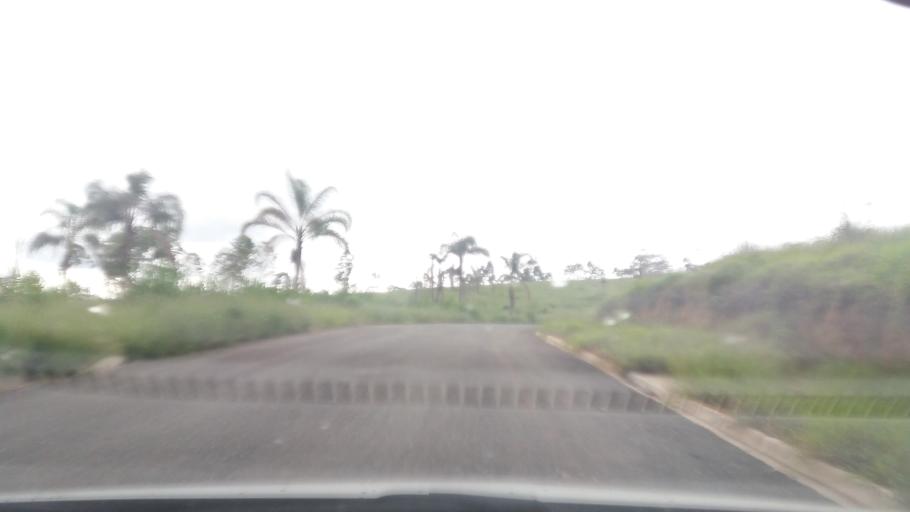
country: BR
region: Sao Paulo
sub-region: Bom Jesus Dos Perdoes
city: Bom Jesus dos Perdoes
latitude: -23.1723
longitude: -46.4385
